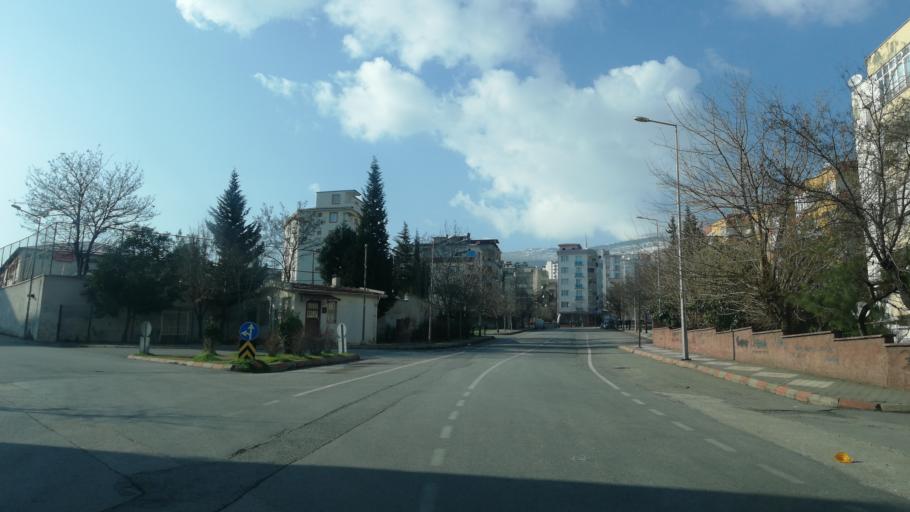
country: TR
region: Kahramanmaras
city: Kahramanmaras
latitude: 37.5891
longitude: 36.9070
